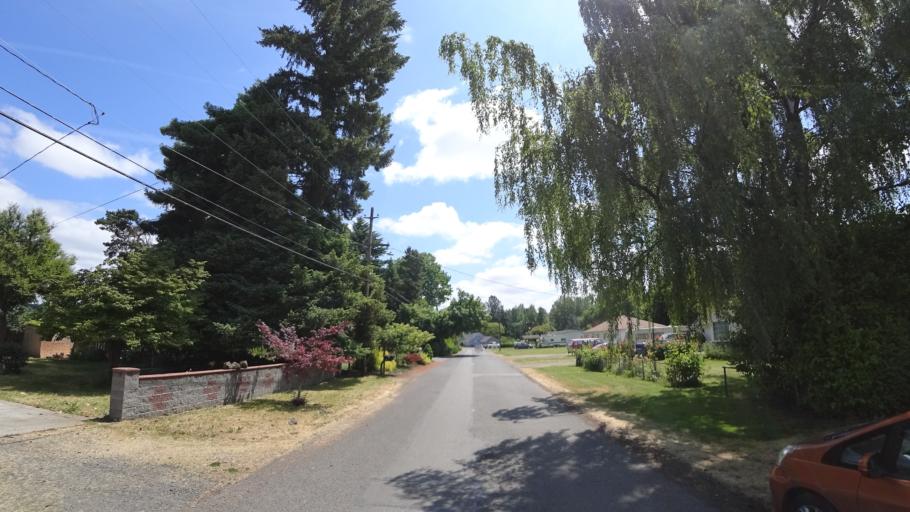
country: US
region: Washington
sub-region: Clark County
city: Vancouver
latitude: 45.5983
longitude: -122.6620
